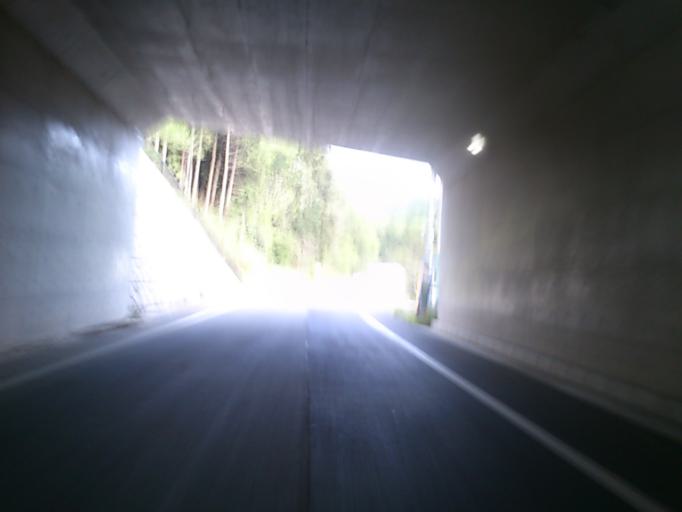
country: JP
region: Kyoto
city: Miyazu
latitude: 35.5672
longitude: 135.1208
